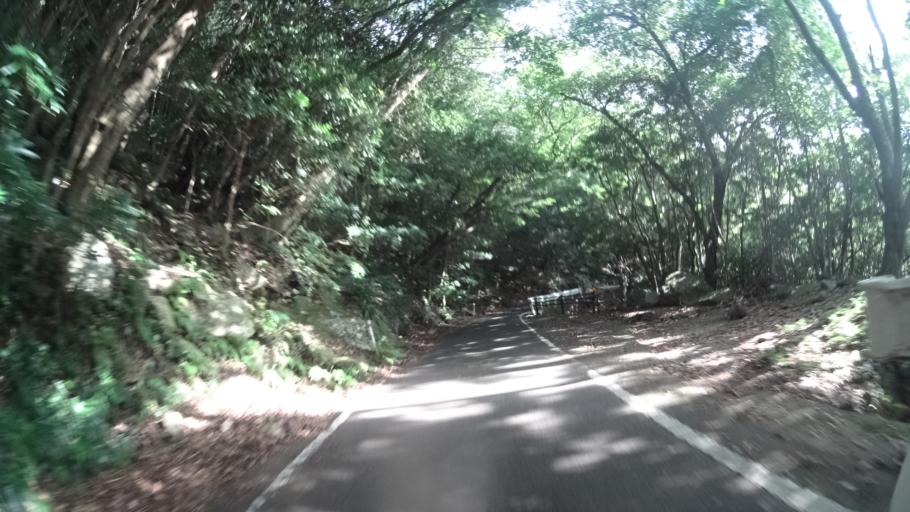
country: JP
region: Kagoshima
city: Nishinoomote
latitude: 30.3374
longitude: 130.3968
